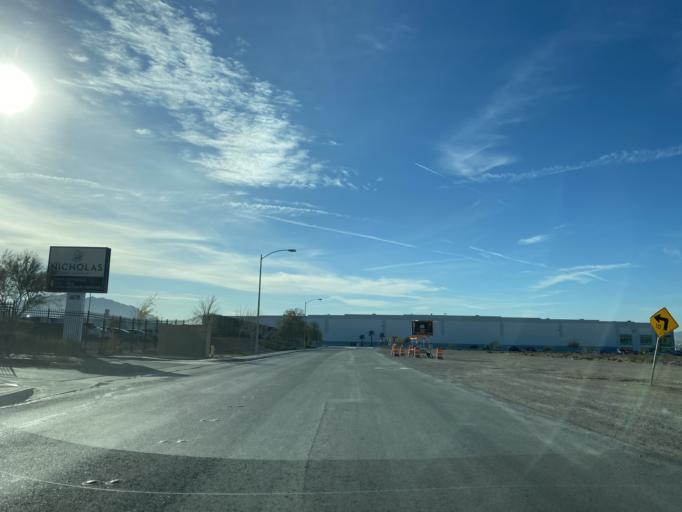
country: US
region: Nevada
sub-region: Clark County
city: Nellis Air Force Base
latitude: 36.2638
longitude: -115.0479
